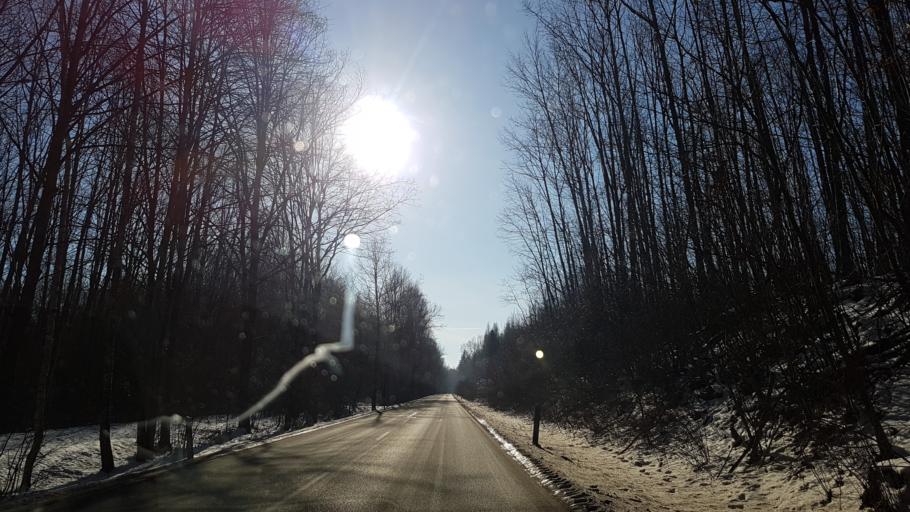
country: DE
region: Thuringia
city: Nobitz
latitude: 50.9668
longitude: 12.5145
